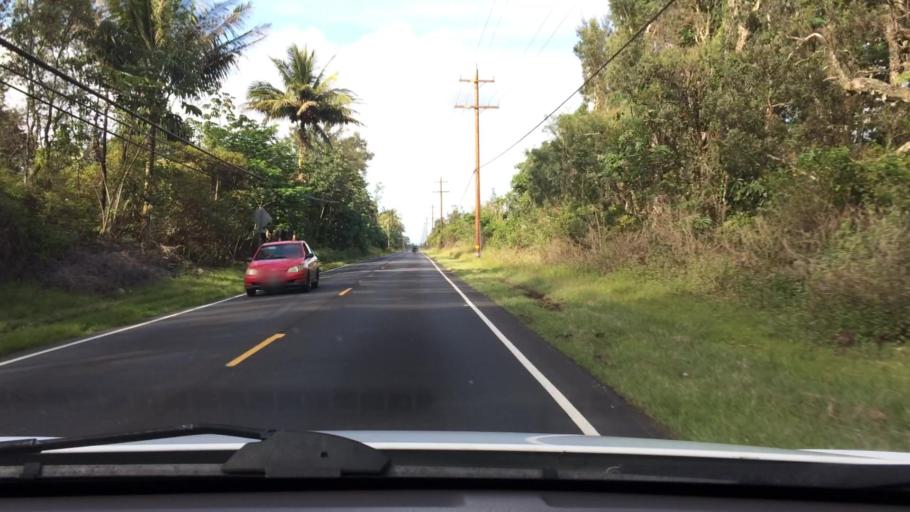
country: US
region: Hawaii
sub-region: Hawaii County
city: Nanawale Estates
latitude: 19.5137
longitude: -154.9409
